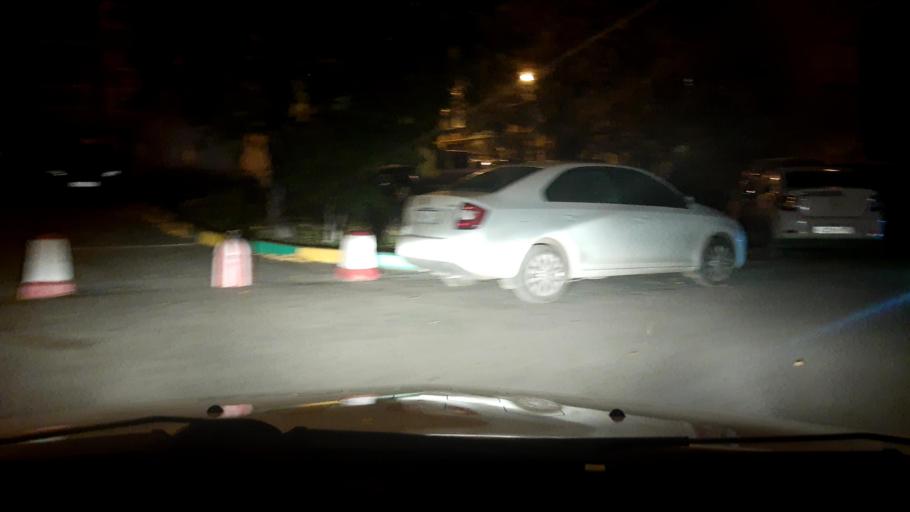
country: RU
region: Bashkortostan
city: Ufa
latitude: 54.7167
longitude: 56.0129
